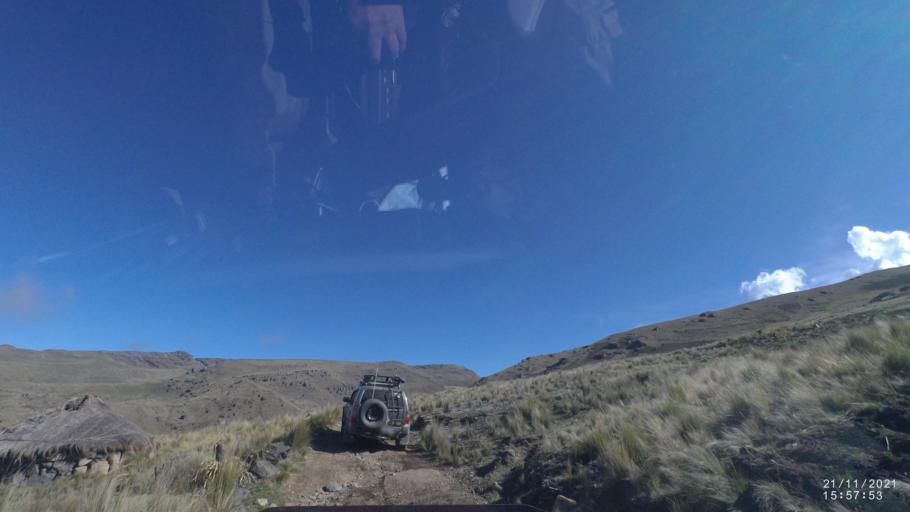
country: BO
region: Cochabamba
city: Cochabamba
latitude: -16.9769
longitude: -66.2638
